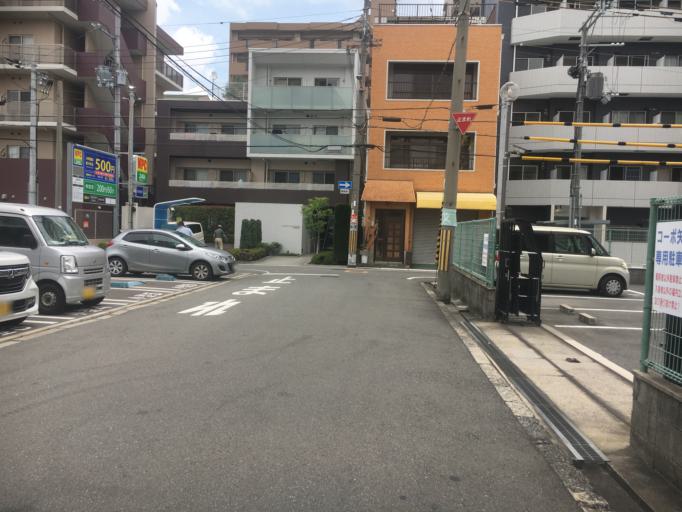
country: JP
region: Osaka
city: Yao
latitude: 34.6539
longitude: 135.5535
